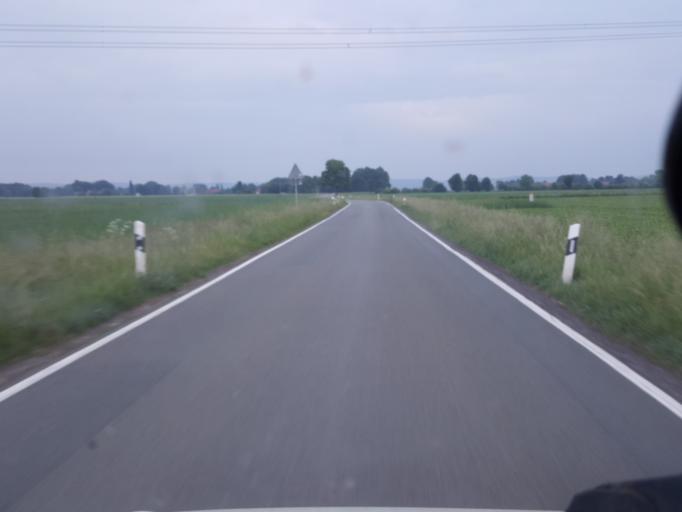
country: DE
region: North Rhine-Westphalia
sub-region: Regierungsbezirk Detmold
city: Minden
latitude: 52.3461
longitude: 8.8476
